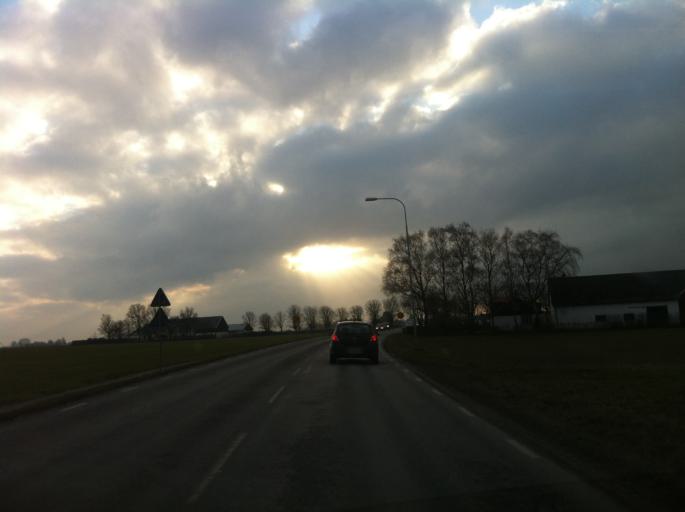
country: SE
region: Skane
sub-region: Kavlinge Kommun
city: Loddekopinge
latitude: 55.7640
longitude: 13.0422
